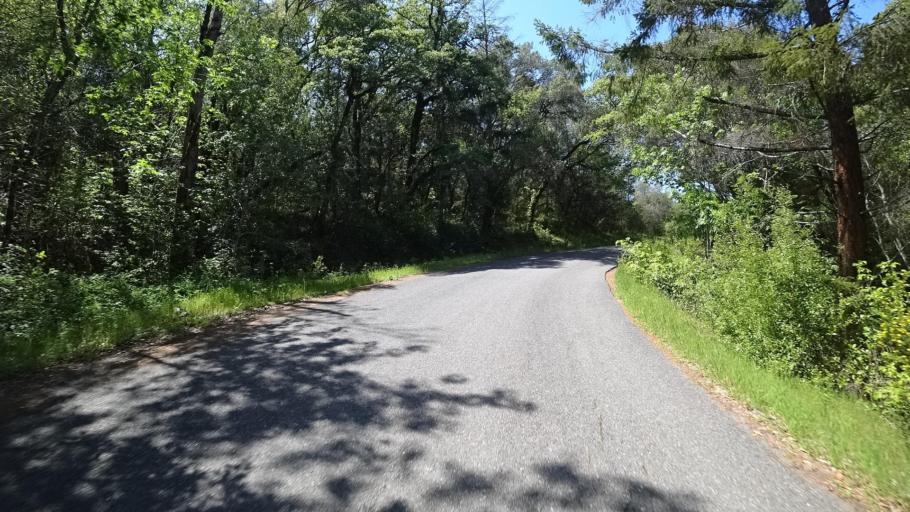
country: US
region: California
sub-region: Humboldt County
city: Redway
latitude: 40.1894
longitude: -123.5669
